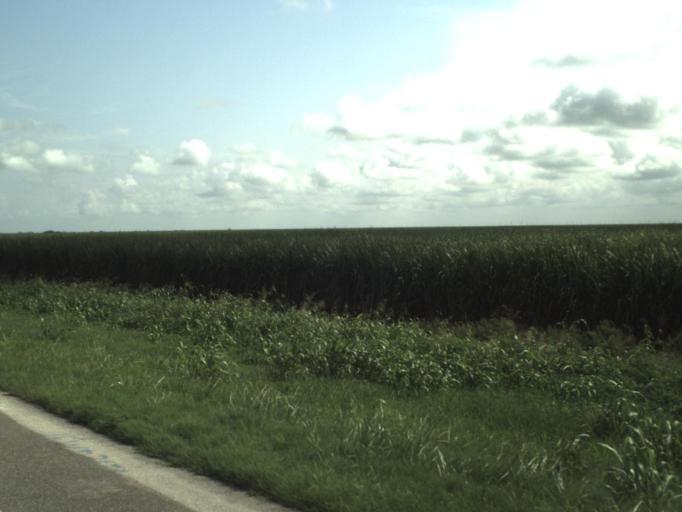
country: US
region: Florida
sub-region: Palm Beach County
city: Belle Glade
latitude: 26.7269
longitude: -80.6840
